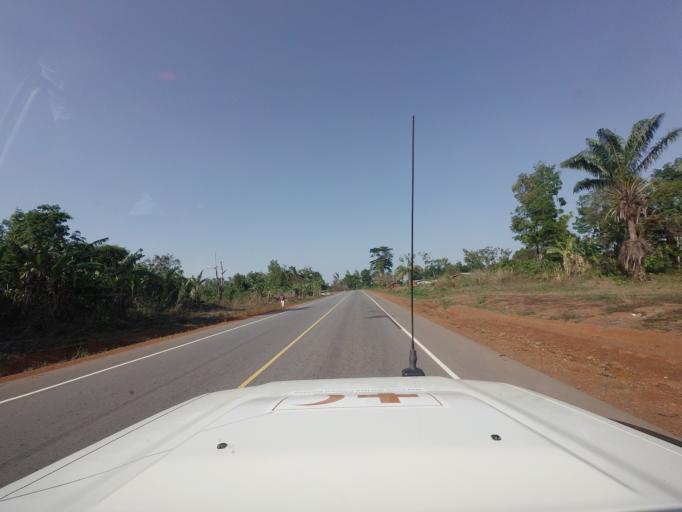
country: LR
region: Nimba
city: Sanniquellie
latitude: 7.1637
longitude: -9.0414
